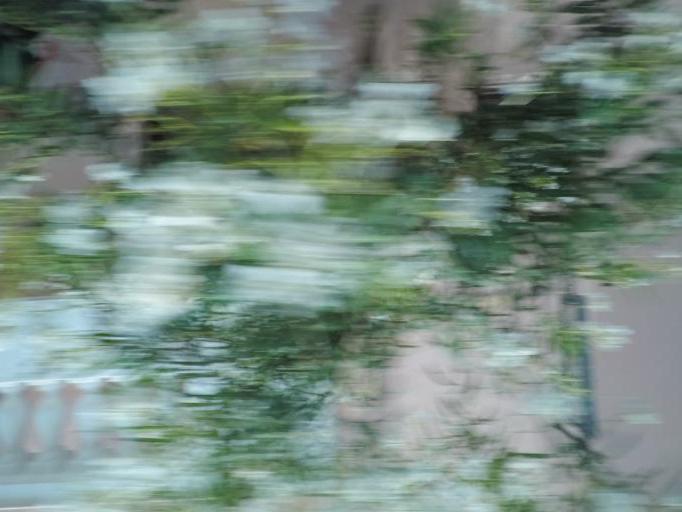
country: GR
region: Crete
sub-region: Nomos Lasithiou
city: Agios Nikolaos
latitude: 35.1895
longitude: 25.7204
